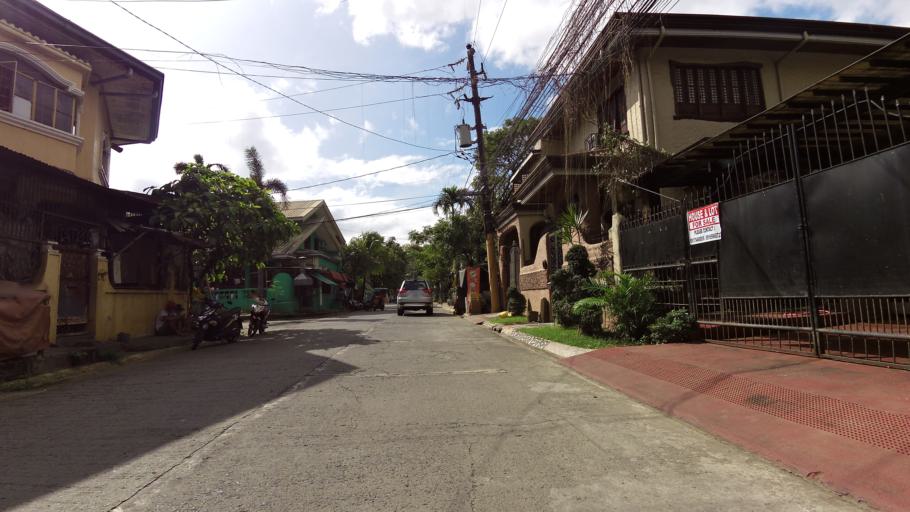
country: PH
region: Calabarzon
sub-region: Province of Rizal
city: Cainta
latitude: 14.5764
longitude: 121.1075
